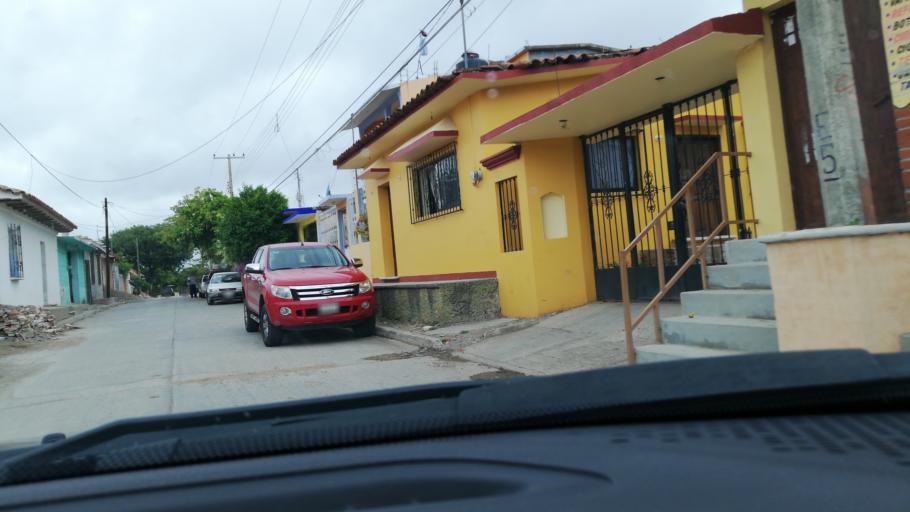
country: MX
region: Oaxaca
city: San Jeronimo Ixtepec
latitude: 16.5649
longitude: -95.1026
